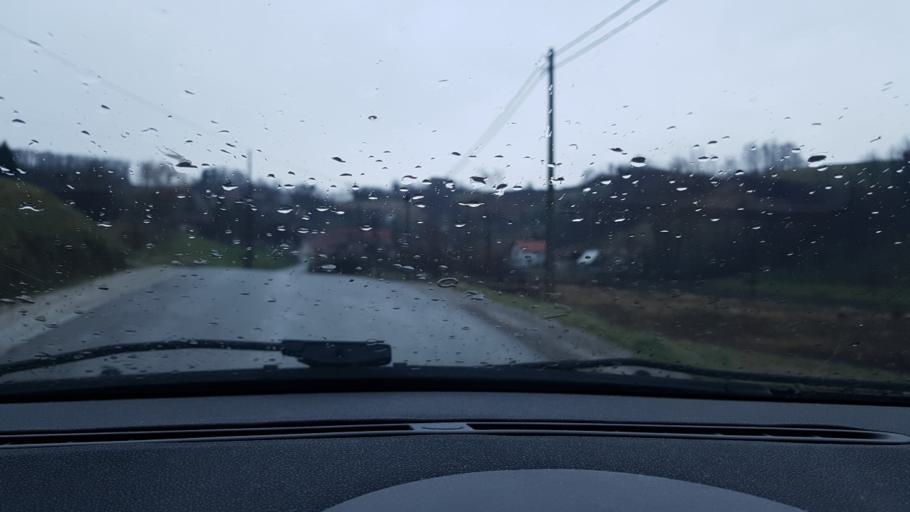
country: HR
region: Krapinsko-Zagorska
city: Bedekovcina
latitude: 45.9892
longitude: 15.9799
